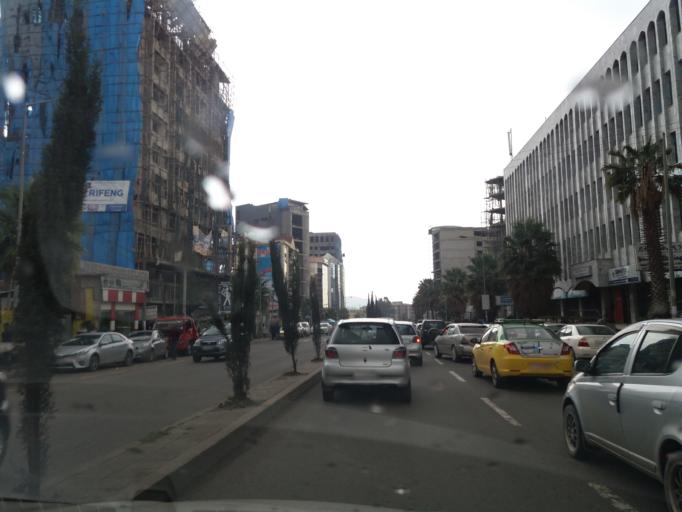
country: ET
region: Adis Abeba
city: Addis Ababa
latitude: 8.9829
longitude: 38.7649
